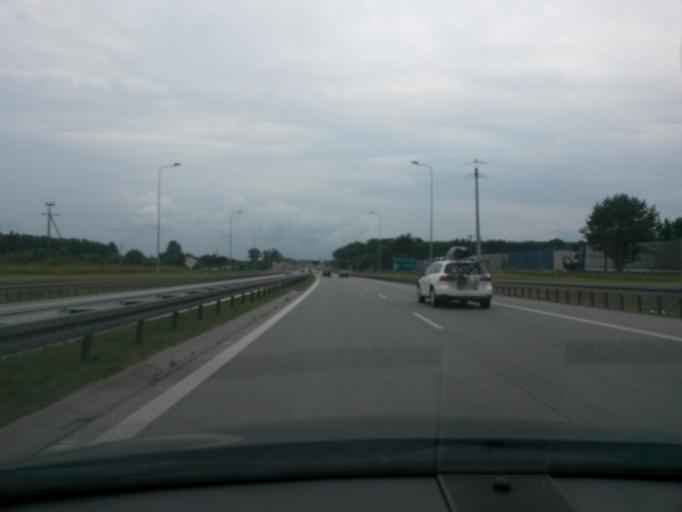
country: PL
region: Lodz Voivodeship
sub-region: Powiat skierniewicki
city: Kowiesy
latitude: 51.9270
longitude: 20.4643
